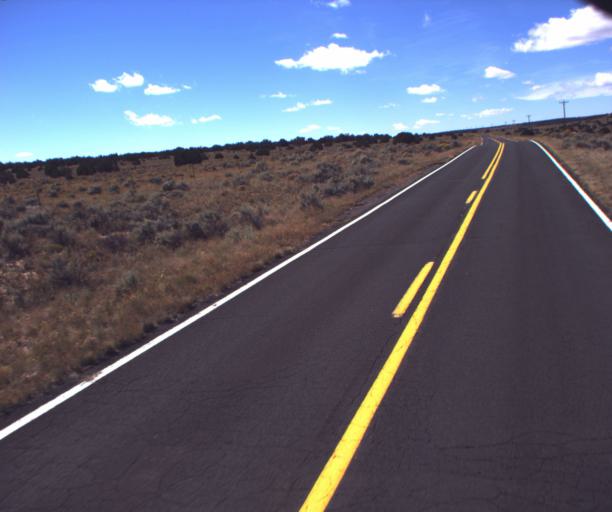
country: US
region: New Mexico
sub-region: McKinley County
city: Zuni Pueblo
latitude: 35.0056
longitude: -109.0798
